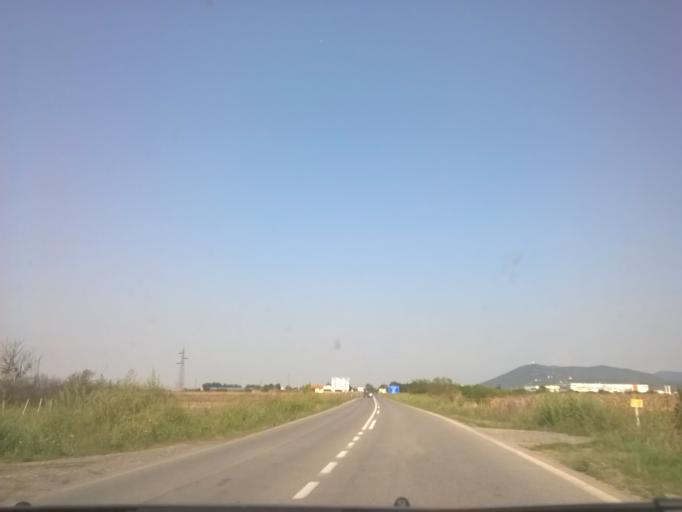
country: RS
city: Pavlis
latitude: 45.0968
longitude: 21.2676
